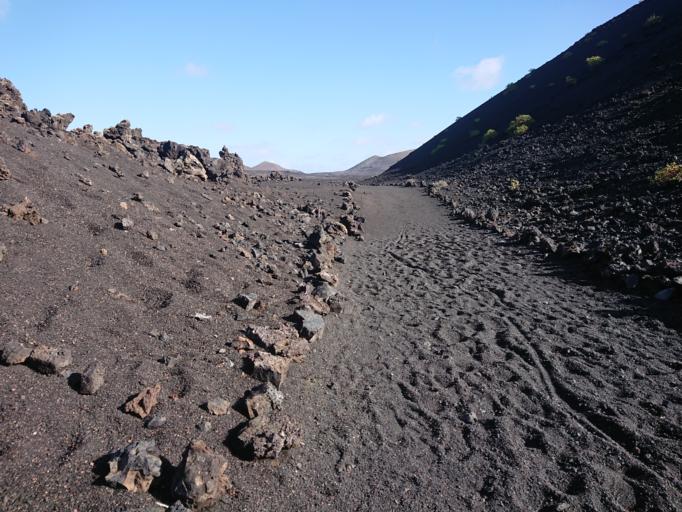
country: ES
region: Canary Islands
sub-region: Provincia de Las Palmas
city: Tias
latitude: 28.9917
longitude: -13.6956
